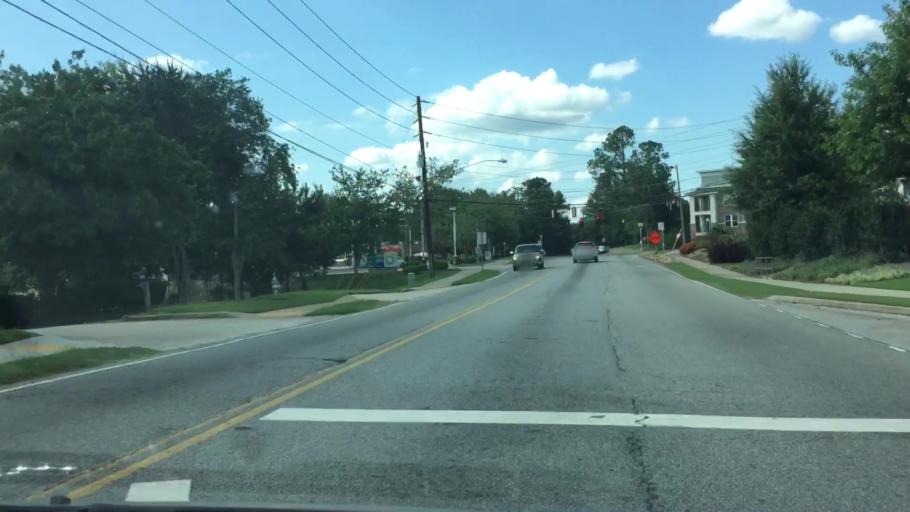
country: US
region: Georgia
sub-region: Fayette County
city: Fayetteville
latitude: 33.4458
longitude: -84.4678
